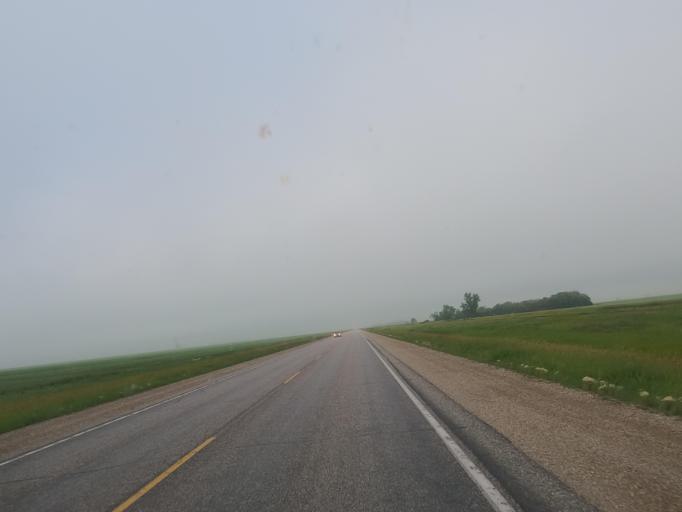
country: CA
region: Manitoba
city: Carman
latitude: 49.7263
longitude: -97.8721
